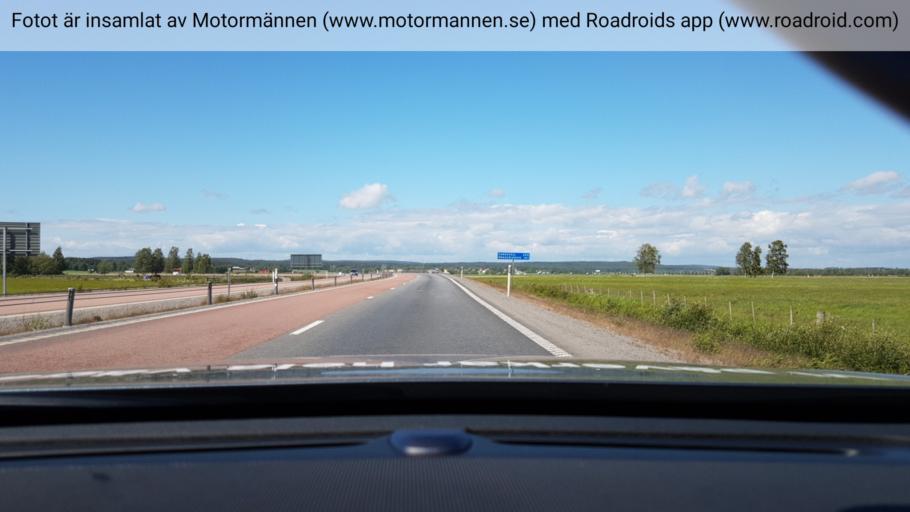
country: SE
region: Vaesterbotten
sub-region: Umea Kommun
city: Umea
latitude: 63.8030
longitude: 20.2509
